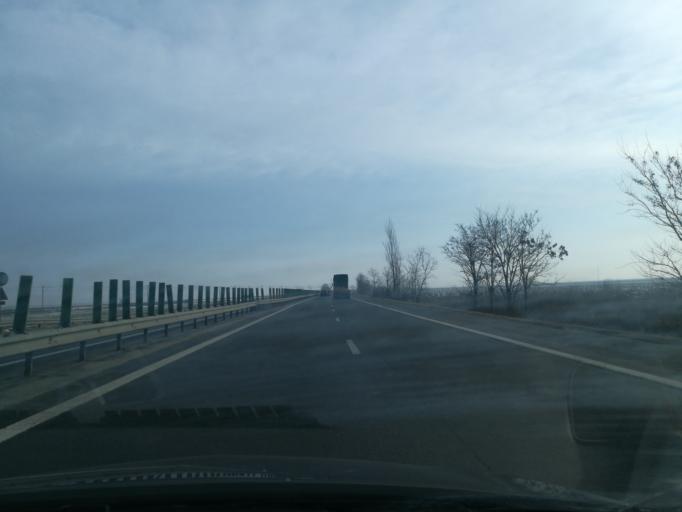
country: RO
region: Calarasi
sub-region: Comuna Nicolae Balcescu
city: Nicolae Balcescu
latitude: 44.4430
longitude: 26.7667
